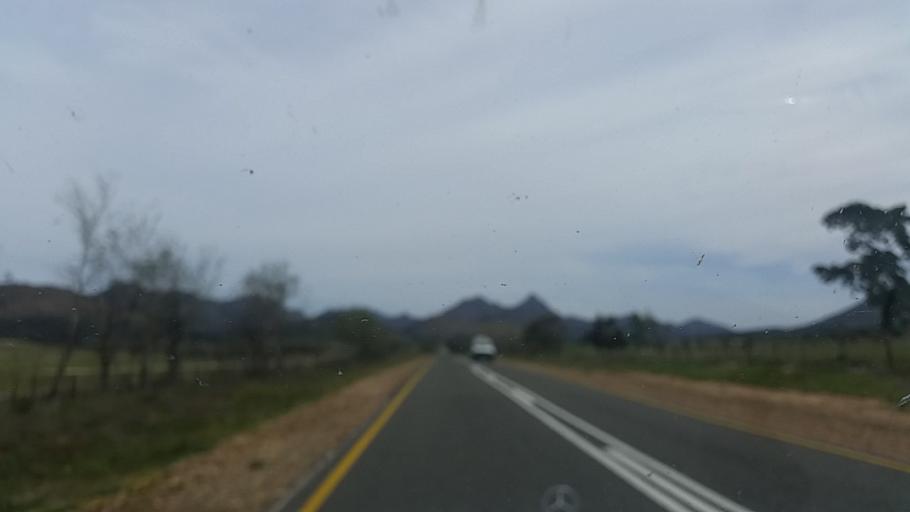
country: ZA
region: Western Cape
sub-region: Eden District Municipality
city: George
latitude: -33.8230
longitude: 22.4858
